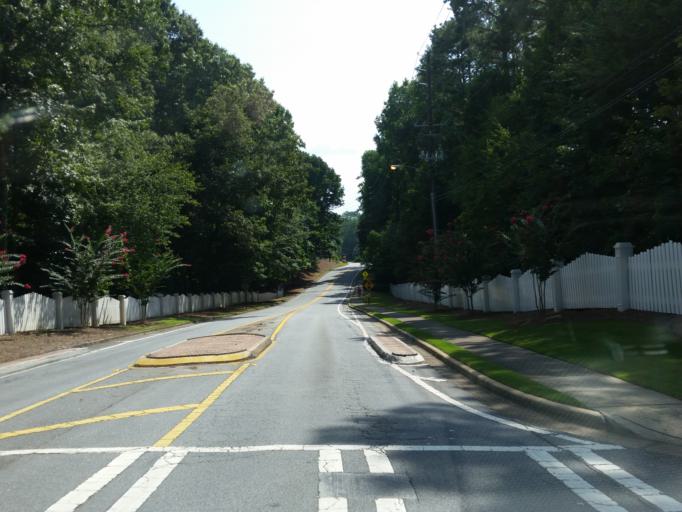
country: US
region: Georgia
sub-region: Fulton County
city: Roswell
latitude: 34.0250
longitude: -84.4473
